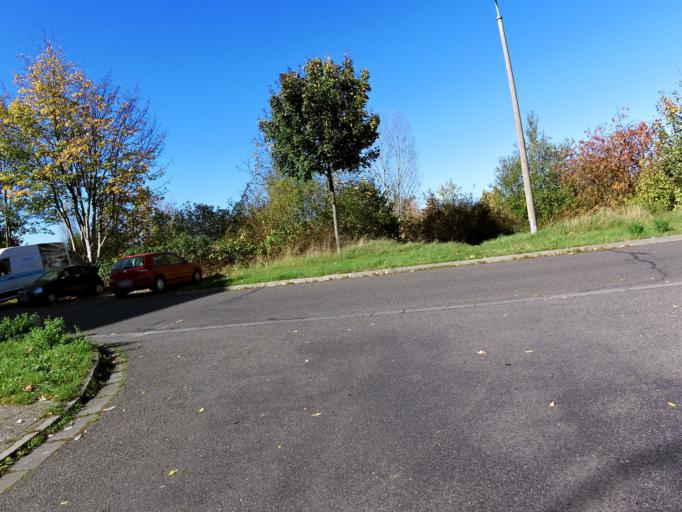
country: DE
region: Saxony
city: Leipzig
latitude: 51.3812
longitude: 12.3614
